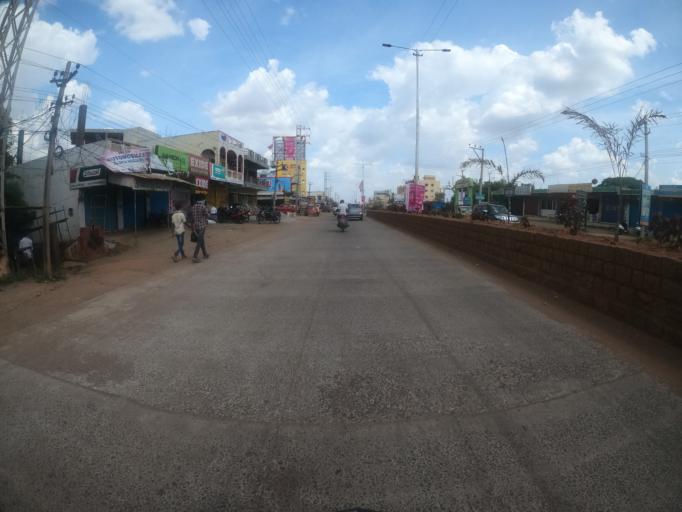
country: IN
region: Telangana
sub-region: Rangareddi
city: Sriramnagar
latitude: 17.3118
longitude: 78.1406
